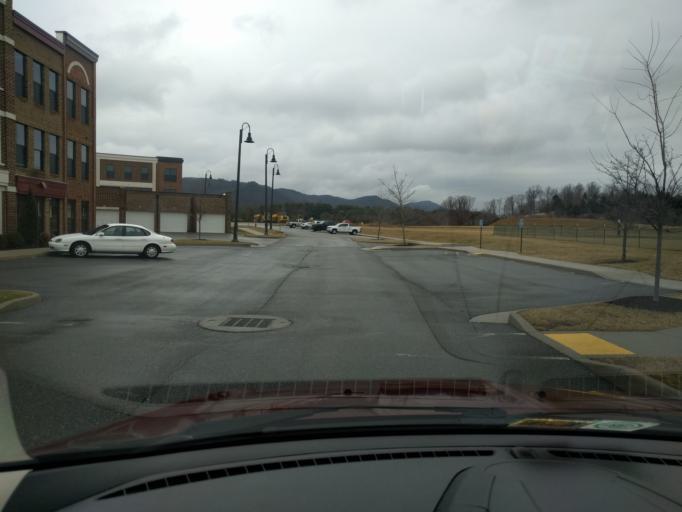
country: US
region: Virginia
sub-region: Botetourt County
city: Daleville
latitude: 37.4165
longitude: -79.9138
